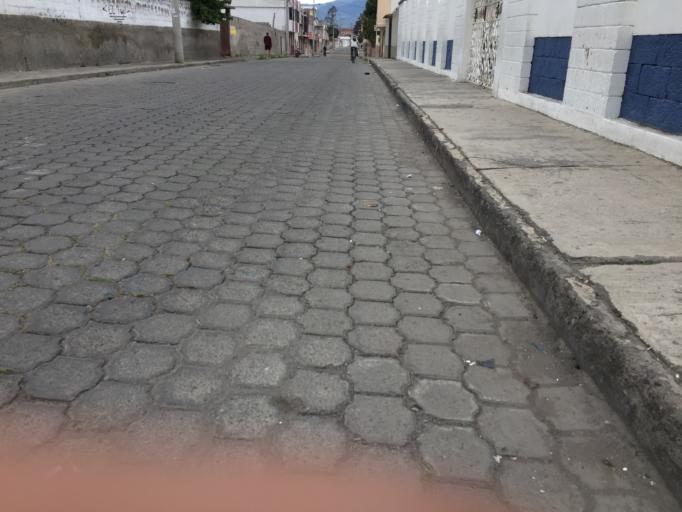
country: EC
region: Imbabura
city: Atuntaqui
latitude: 0.3297
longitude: -78.2217
